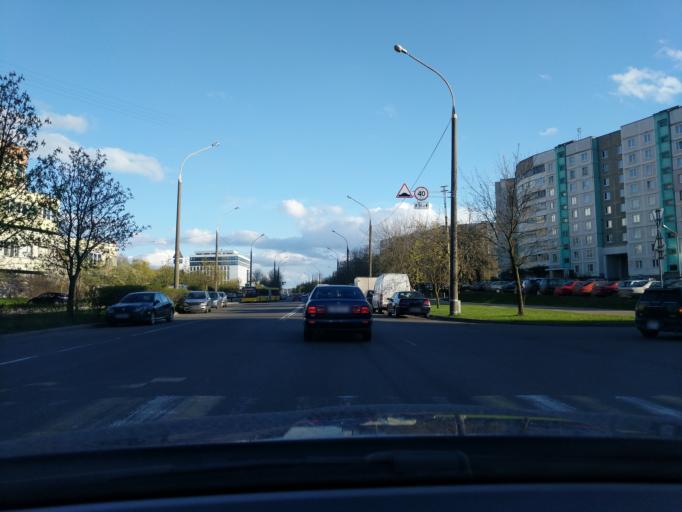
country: BY
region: Minsk
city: Novoye Medvezhino
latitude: 53.9126
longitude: 27.4506
